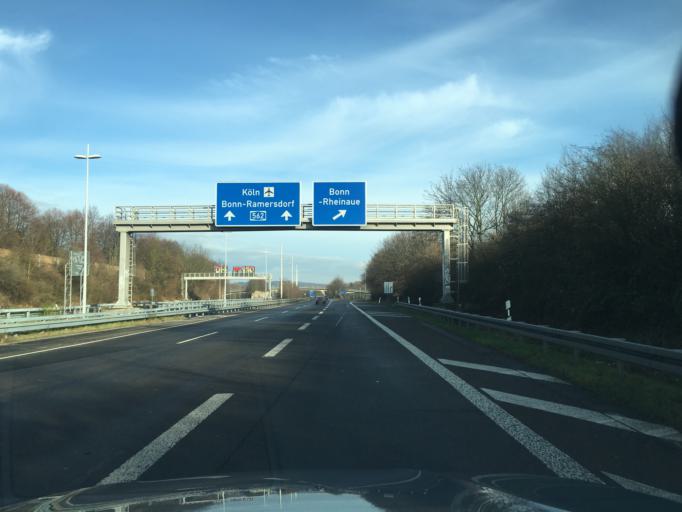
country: DE
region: North Rhine-Westphalia
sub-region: Regierungsbezirk Koln
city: Bonn
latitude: 50.7072
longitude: 7.1347
